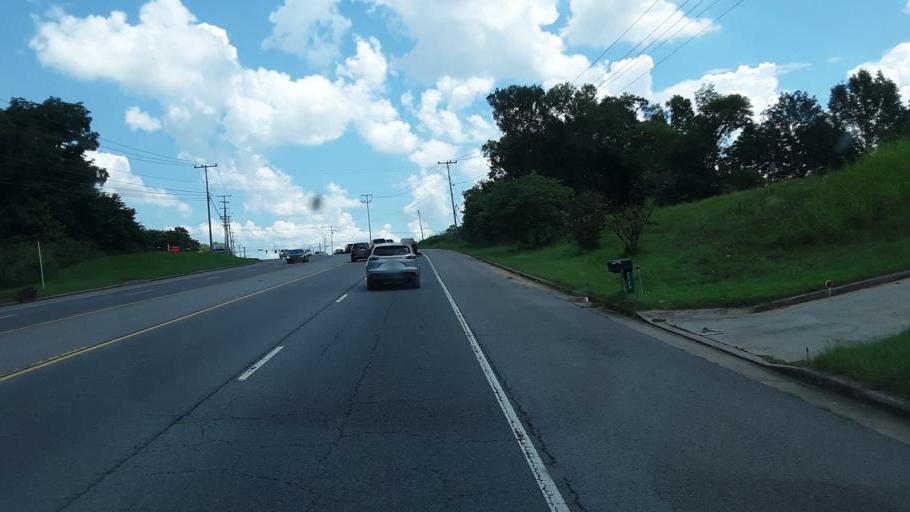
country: US
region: Kentucky
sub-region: Christian County
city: Oak Grove
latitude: 36.6265
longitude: -87.3625
